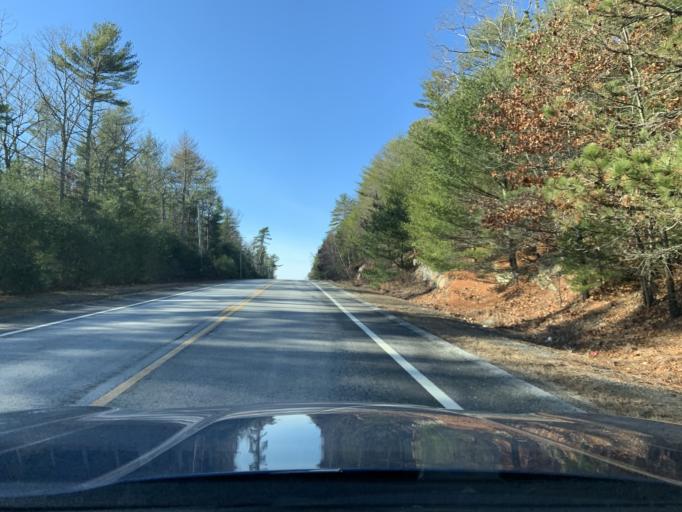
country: US
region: Rhode Island
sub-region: Kent County
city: West Greenwich
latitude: 41.5773
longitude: -71.6916
